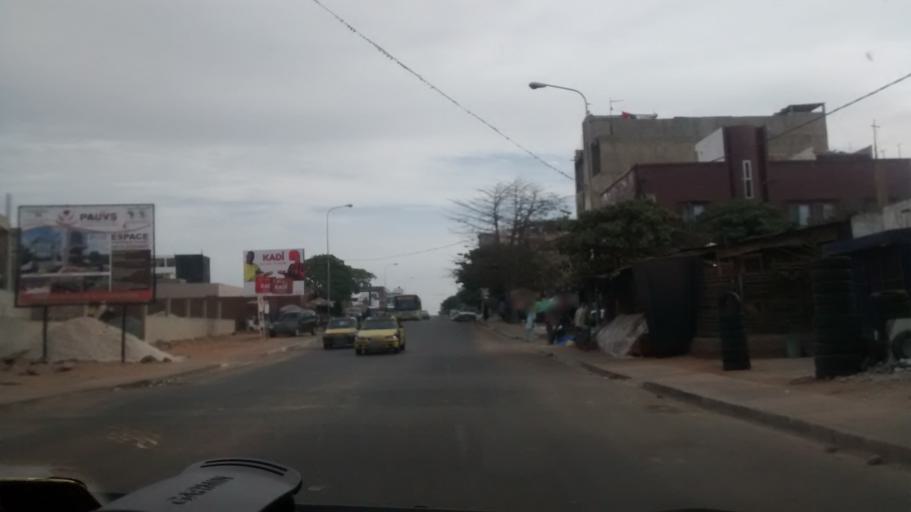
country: SN
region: Dakar
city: Pikine
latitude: 14.7831
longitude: -17.3846
